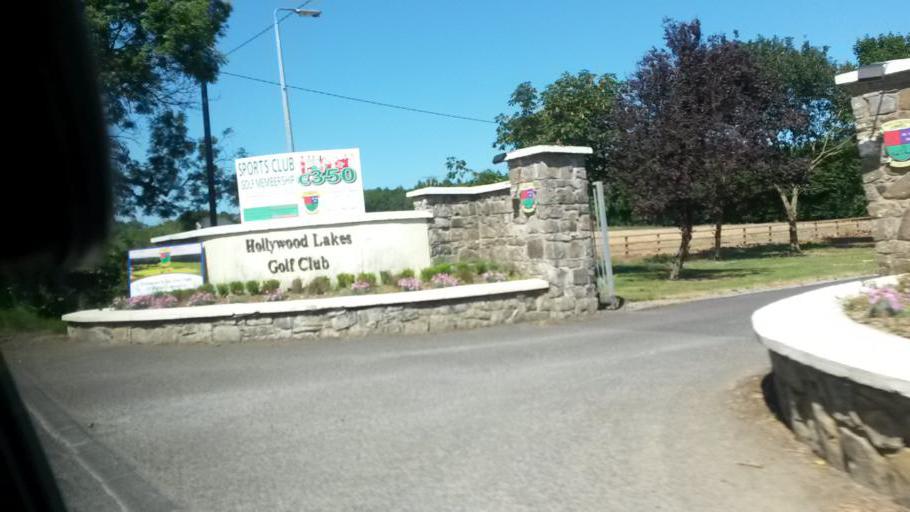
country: IE
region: Leinster
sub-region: An Mhi
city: Stamullin
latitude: 53.5526
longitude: -6.2724
